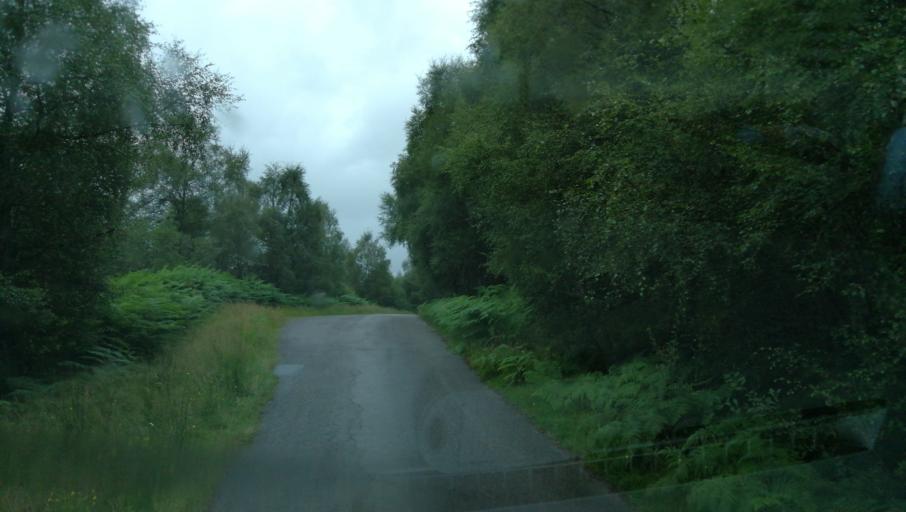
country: GB
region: Scotland
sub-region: Highland
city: Spean Bridge
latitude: 57.2659
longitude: -4.9828
